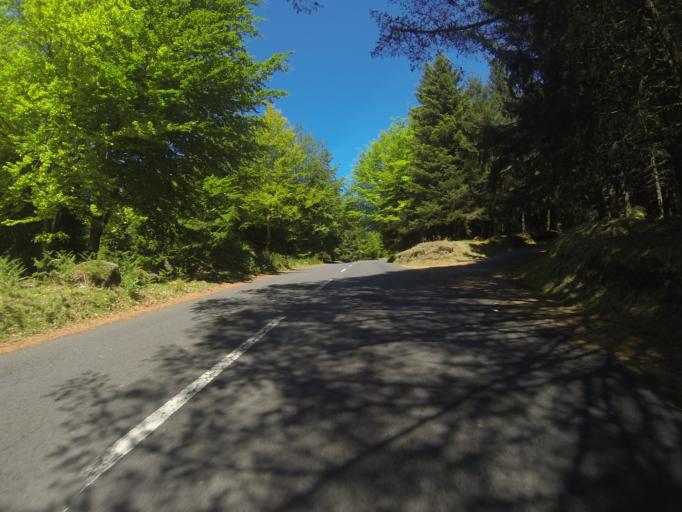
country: PT
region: Madeira
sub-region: Funchal
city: Nossa Senhora do Monte
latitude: 32.7225
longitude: -16.8863
